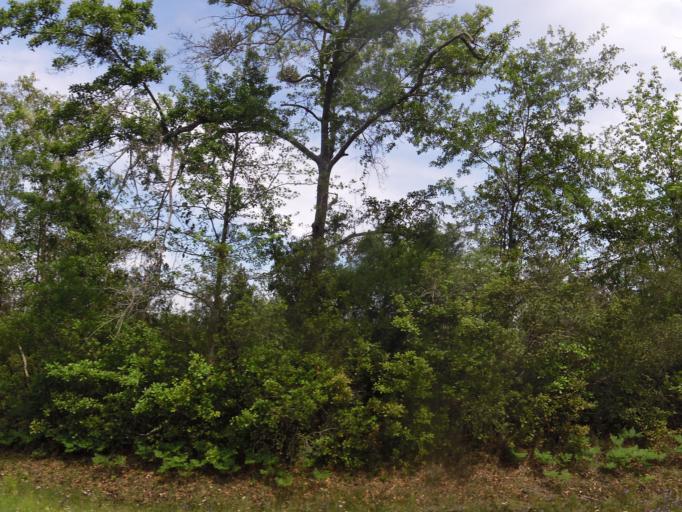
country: US
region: Georgia
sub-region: Camden County
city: Kingsland
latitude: 30.7624
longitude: -81.6589
